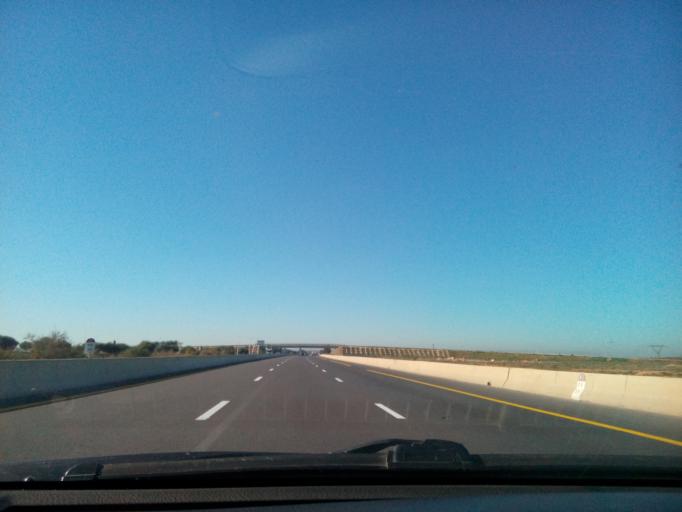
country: DZ
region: Relizane
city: Djidiouia
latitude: 35.9181
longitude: 0.7637
